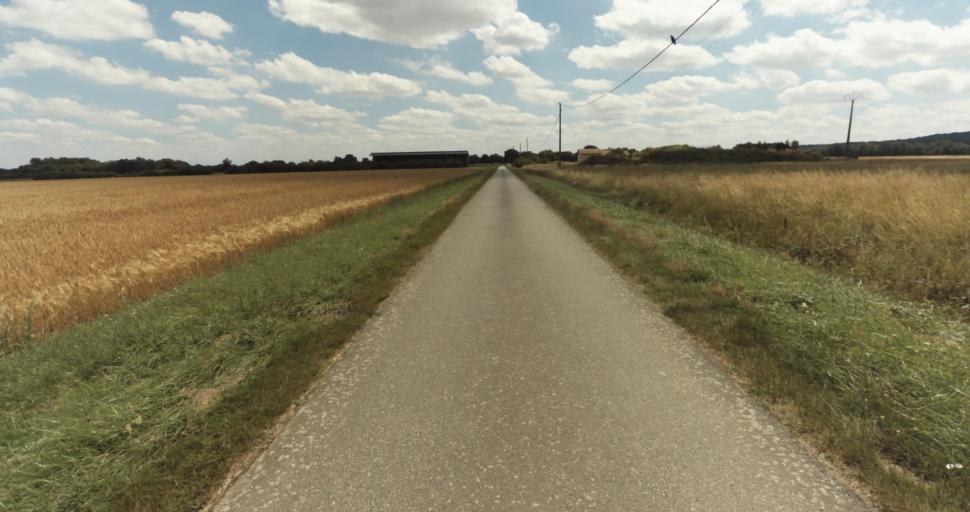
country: FR
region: Midi-Pyrenees
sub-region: Departement de la Haute-Garonne
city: Fontenilles
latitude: 43.5668
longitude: 1.1790
